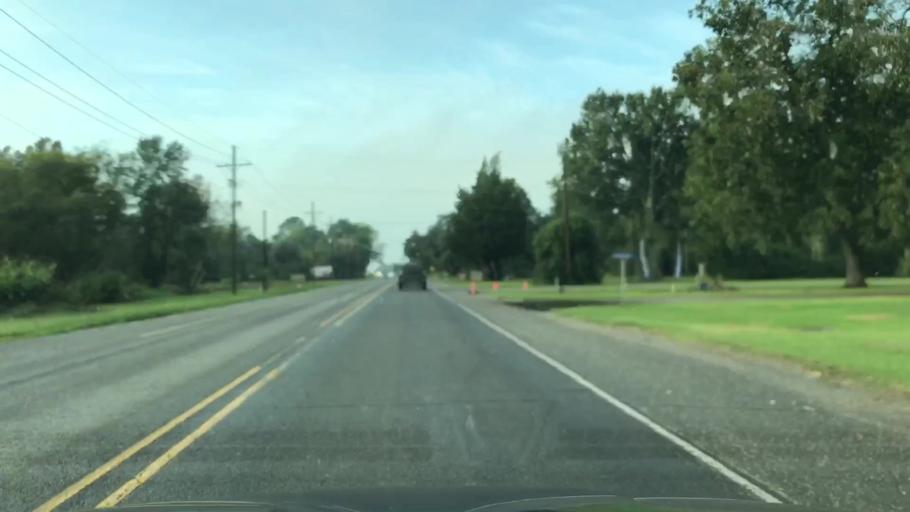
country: US
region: Louisiana
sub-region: Terrebonne Parish
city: Gray
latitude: 29.6749
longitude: -90.8144
